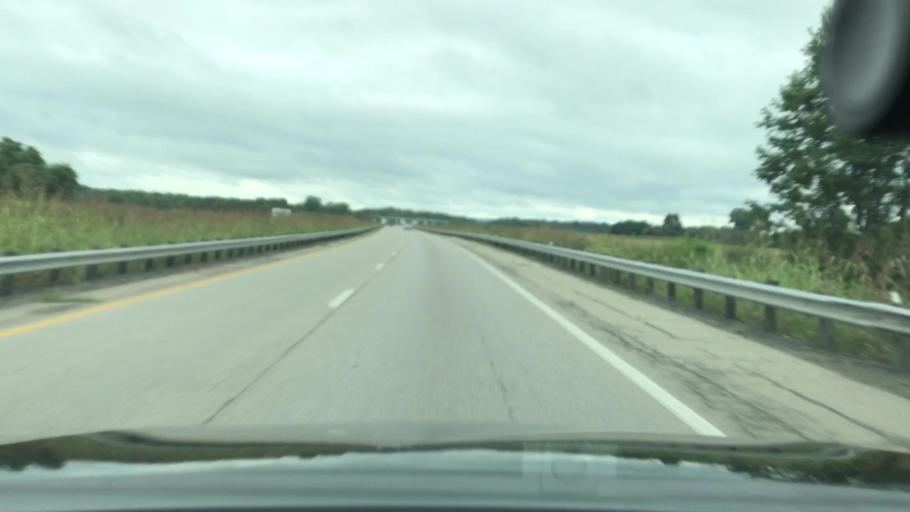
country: US
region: Ohio
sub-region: Ross County
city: Chillicothe
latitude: 39.3200
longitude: -82.9380
